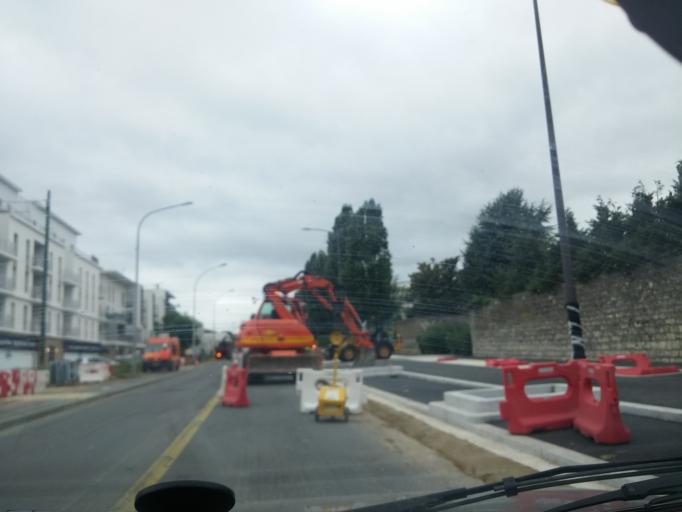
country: FR
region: Ile-de-France
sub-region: Departement du Val-de-Marne
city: Thiais
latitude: 48.7669
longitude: 2.3834
